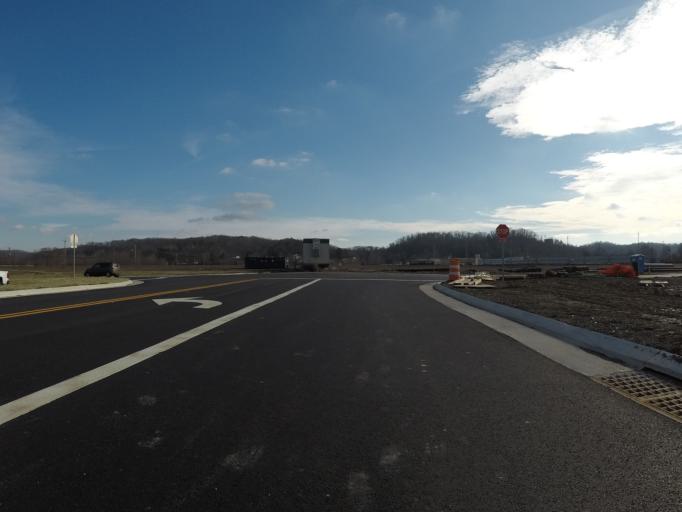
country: US
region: West Virginia
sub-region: Cabell County
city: Barboursville
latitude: 38.4137
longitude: -82.2894
